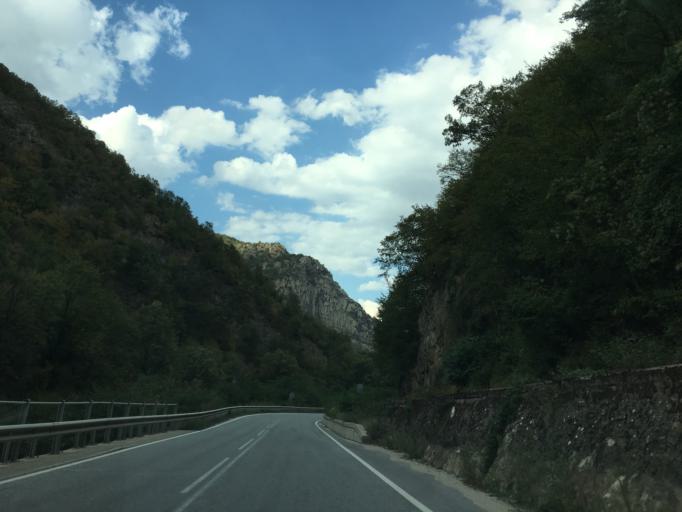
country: BG
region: Pazardzhik
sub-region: Obshtina Septemvri
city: Septemvri
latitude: 42.1039
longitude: 24.1032
